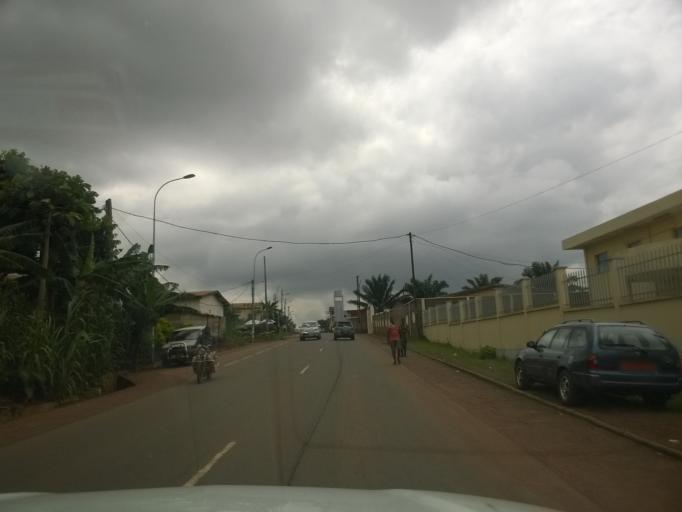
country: CM
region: Centre
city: Yaounde
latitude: 3.8521
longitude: 11.5057
